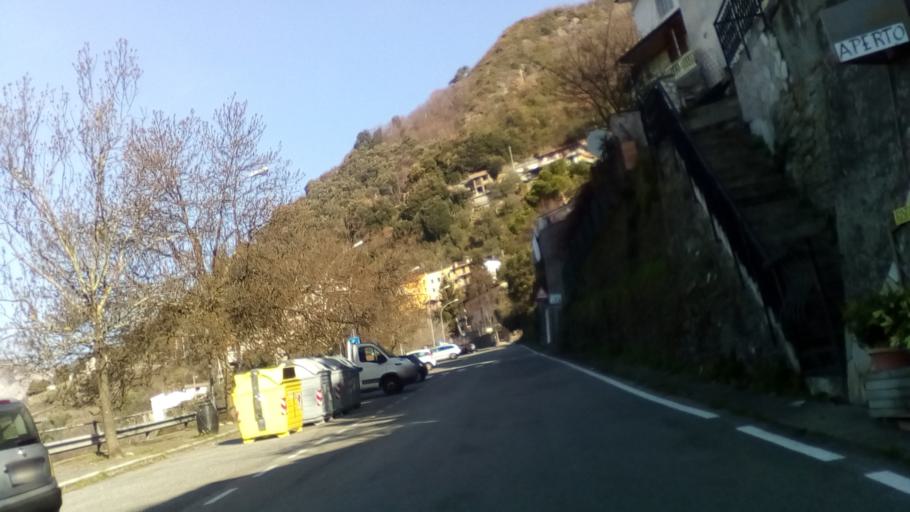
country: IT
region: Tuscany
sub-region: Provincia di Massa-Carrara
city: Montignoso
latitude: 44.0573
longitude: 10.1816
